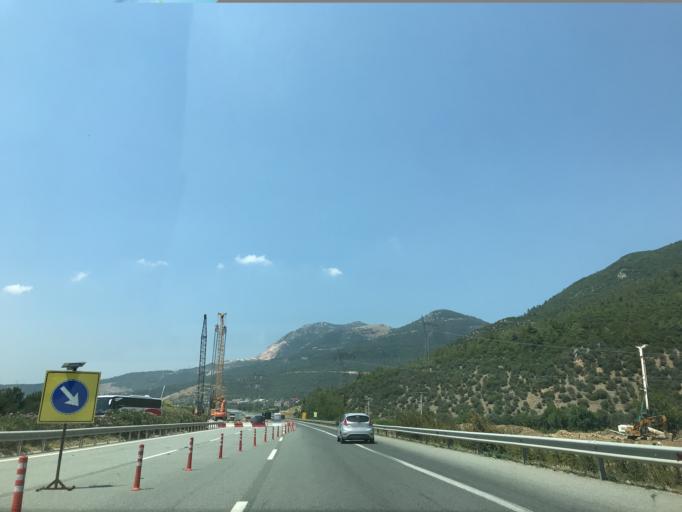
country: TR
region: Bursa
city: Kestel
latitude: 40.2396
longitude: 29.2617
